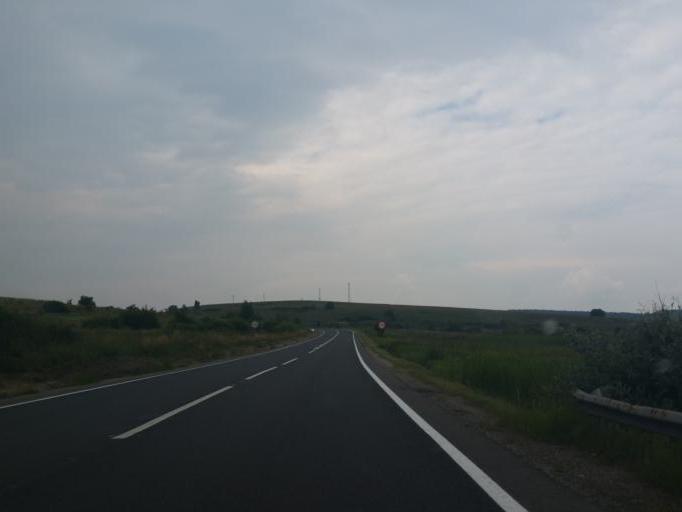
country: RO
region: Cluj
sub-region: Comuna Sanpaul
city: Sanpaul
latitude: 46.9246
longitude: 23.4079
